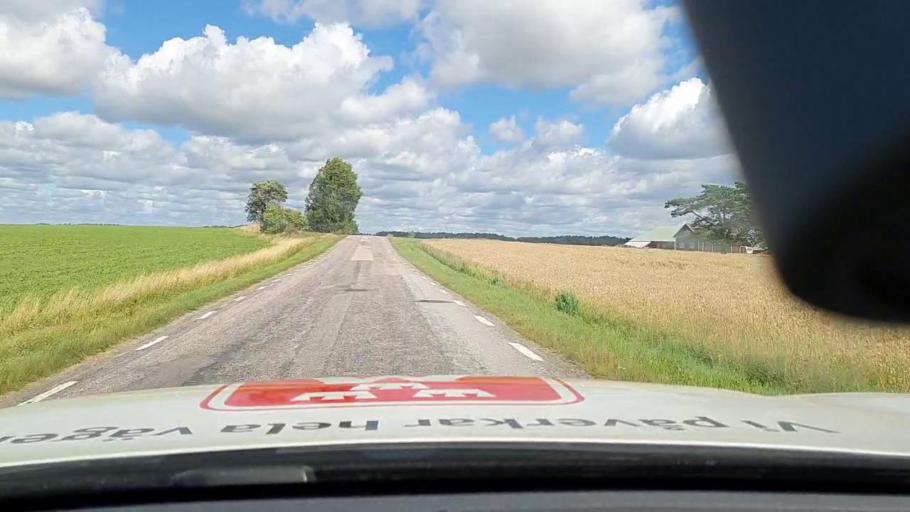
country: SE
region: Vaestra Goetaland
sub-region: Toreboda Kommun
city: Toereboda
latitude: 58.5812
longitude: 14.0977
